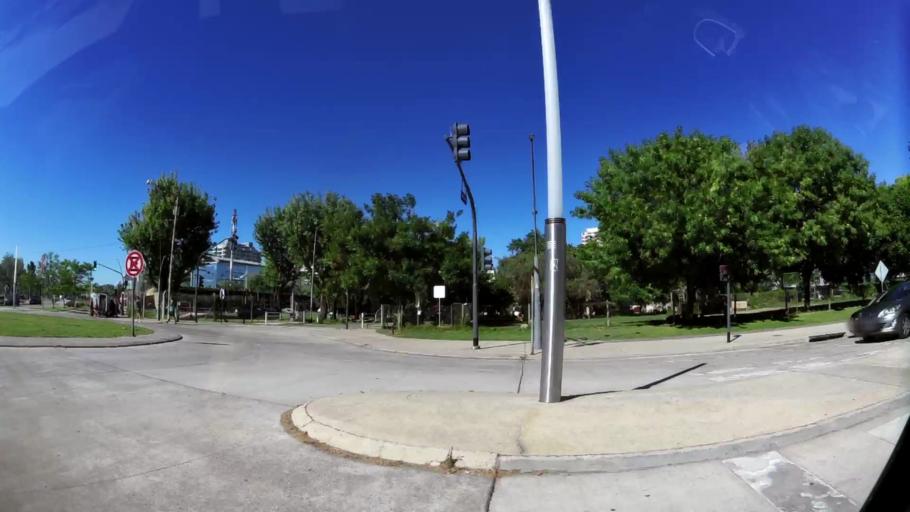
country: AR
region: Buenos Aires
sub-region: Partido de Vicente Lopez
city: Olivos
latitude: -34.5181
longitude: -58.4716
